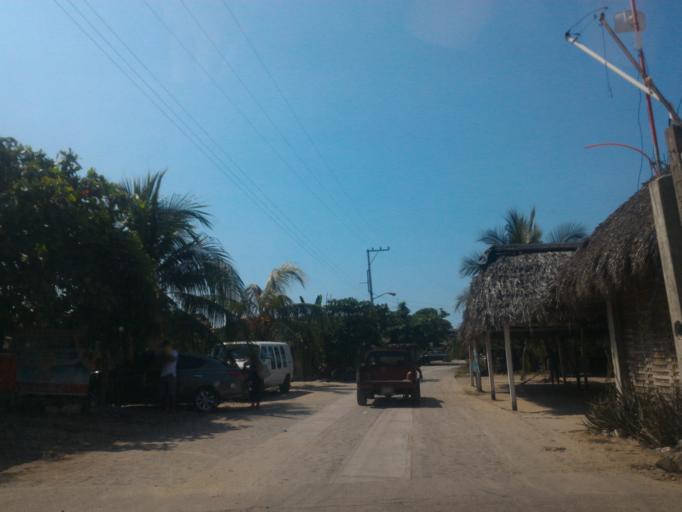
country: MX
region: Michoacan
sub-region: Coalcoman de Vazquez Pallares
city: Coalcoman de Vazquez Pallares
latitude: 18.2708
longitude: -103.3462
